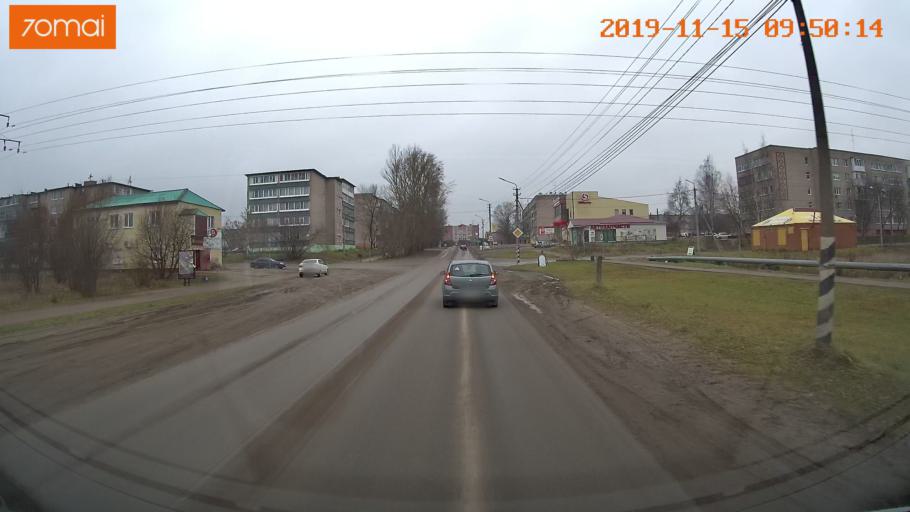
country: RU
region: Vologda
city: Sheksna
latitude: 59.2319
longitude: 38.5128
